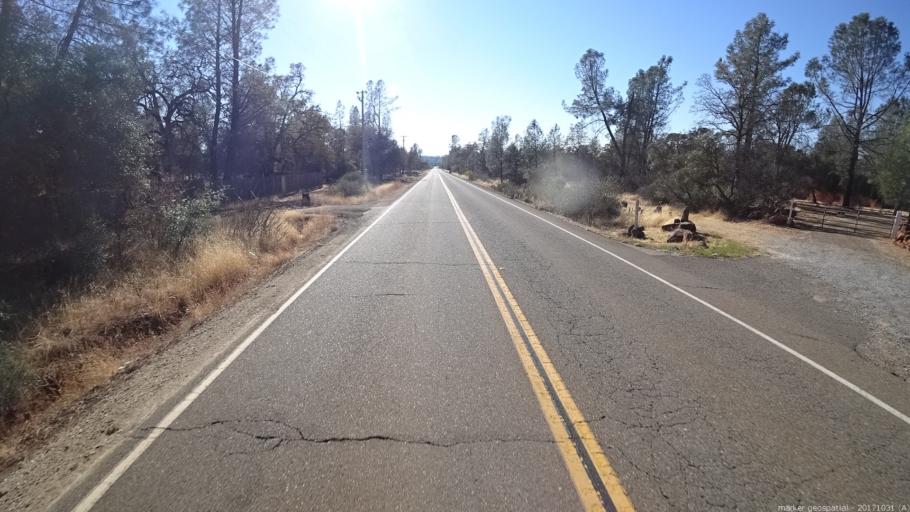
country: US
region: California
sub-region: Shasta County
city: Shingletown
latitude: 40.4970
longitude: -122.0453
